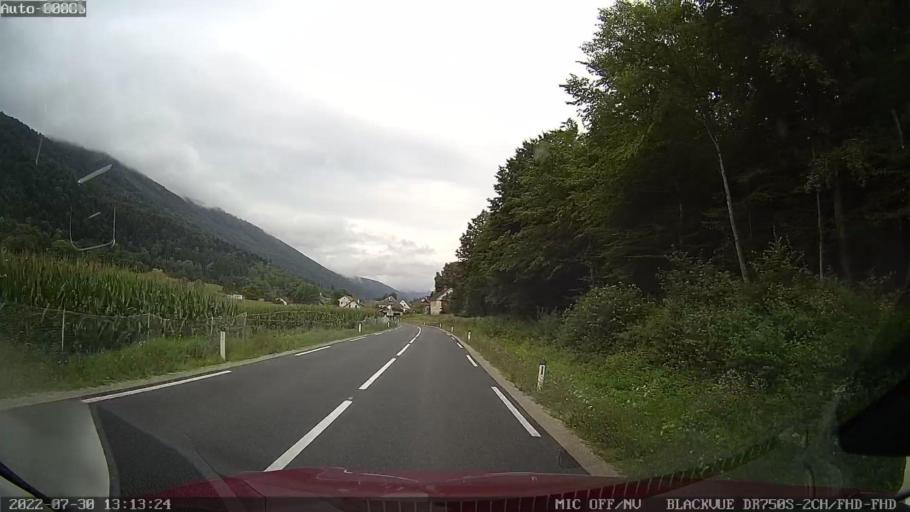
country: SI
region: Dolenjske Toplice
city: Dolenjske Toplice
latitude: 45.7208
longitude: 15.0582
